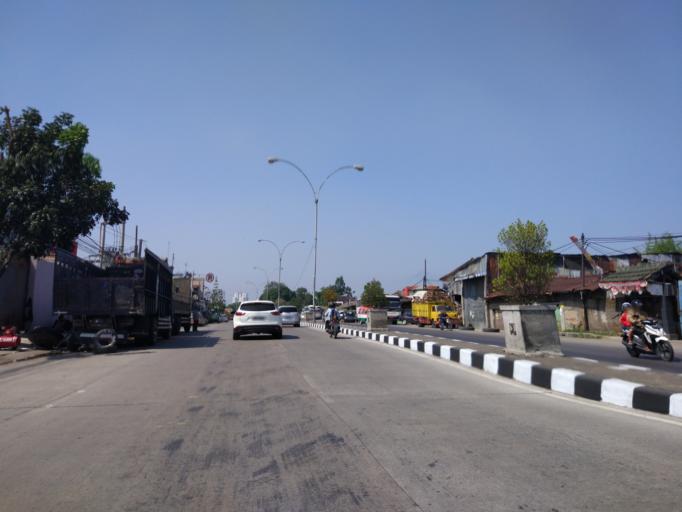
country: ID
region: West Java
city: Margahayukencana
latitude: -6.9388
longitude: 107.5806
